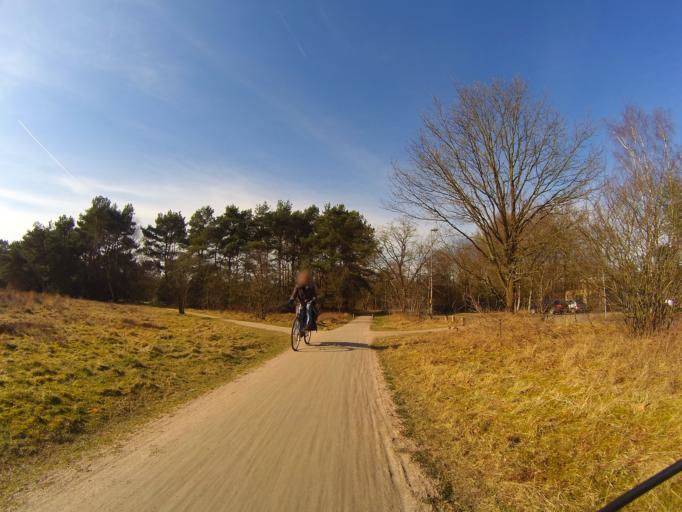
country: NL
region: North Holland
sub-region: Gemeente Bussum
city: Bussum
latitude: 52.2644
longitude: 5.1577
